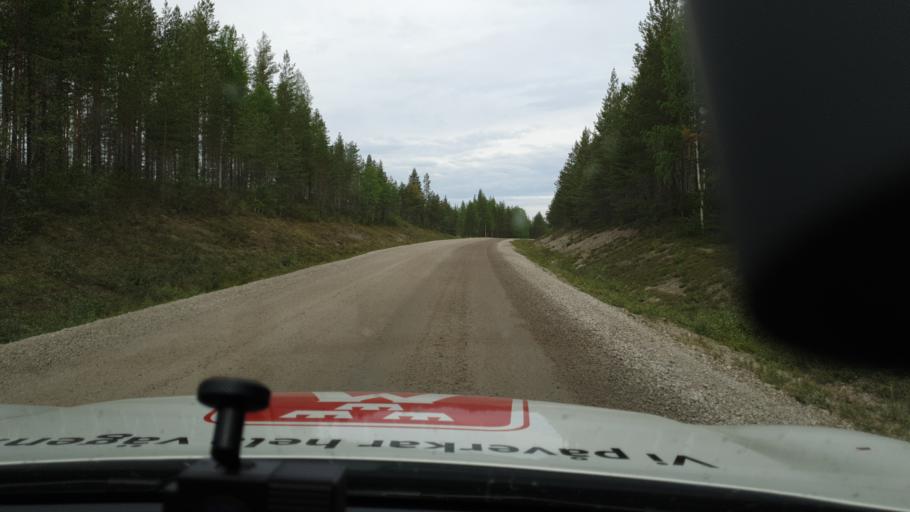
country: SE
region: Vaesterbotten
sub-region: Lycksele Kommun
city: Lycksele
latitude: 64.8527
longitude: 18.7513
